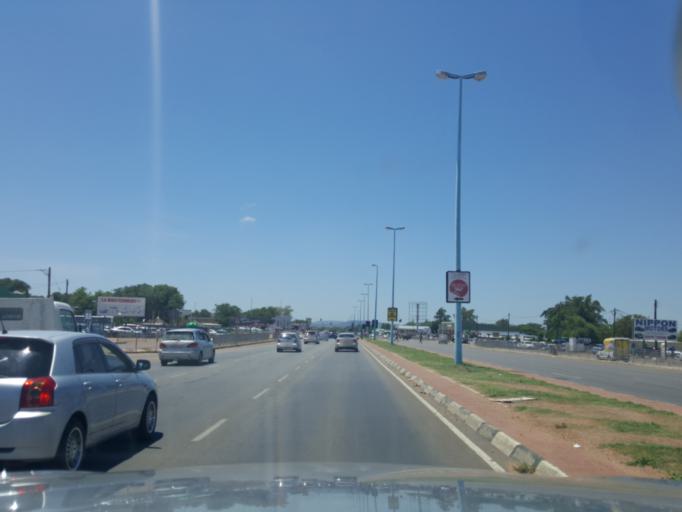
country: BW
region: Kweneng
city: Mogoditshane
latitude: -24.6266
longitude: 25.8704
